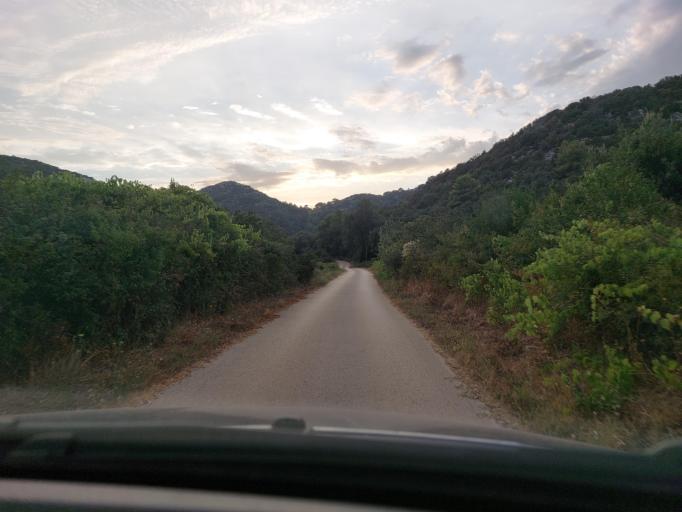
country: HR
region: Dubrovacko-Neretvanska
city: Smokvica
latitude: 42.7556
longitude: 16.9191
